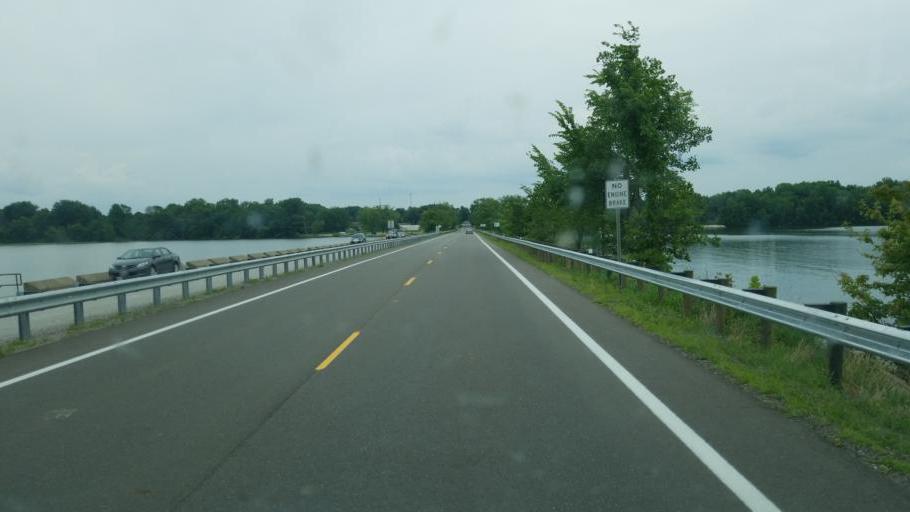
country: US
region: Ohio
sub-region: Trumbull County
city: Cortland
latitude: 41.3898
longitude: -80.7466
